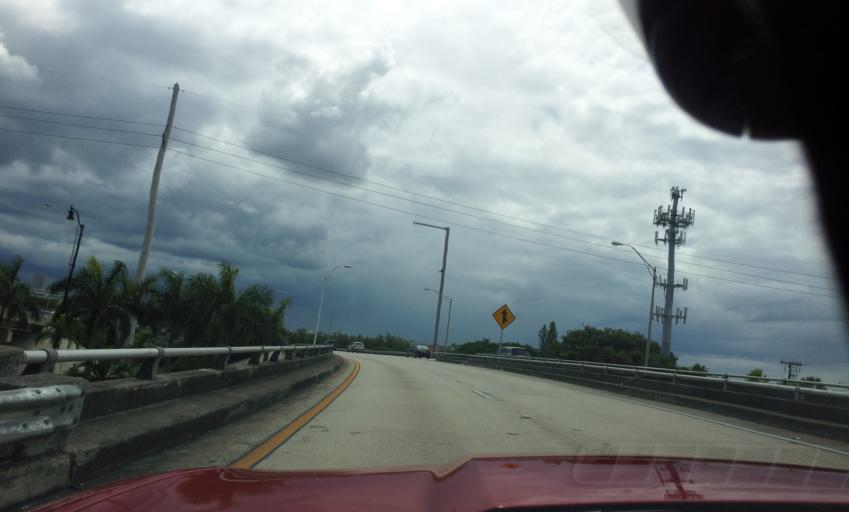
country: US
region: Florida
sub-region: Miami-Dade County
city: Allapattah
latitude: 25.8101
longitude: -80.2064
